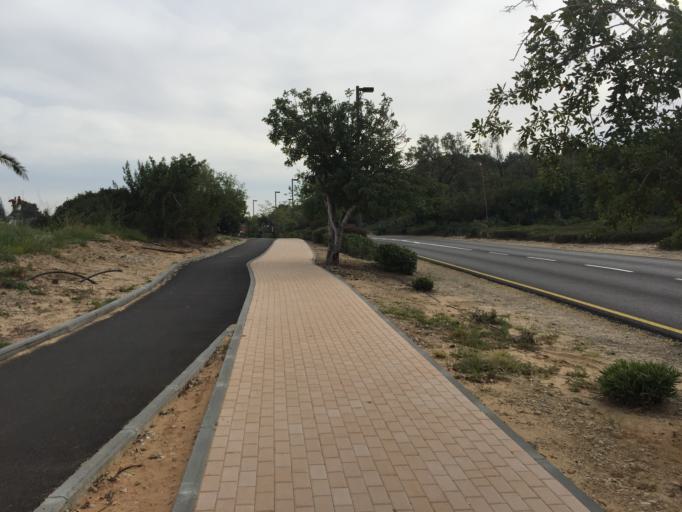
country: IL
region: Haifa
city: Qesarya
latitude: 32.5084
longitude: 34.9040
